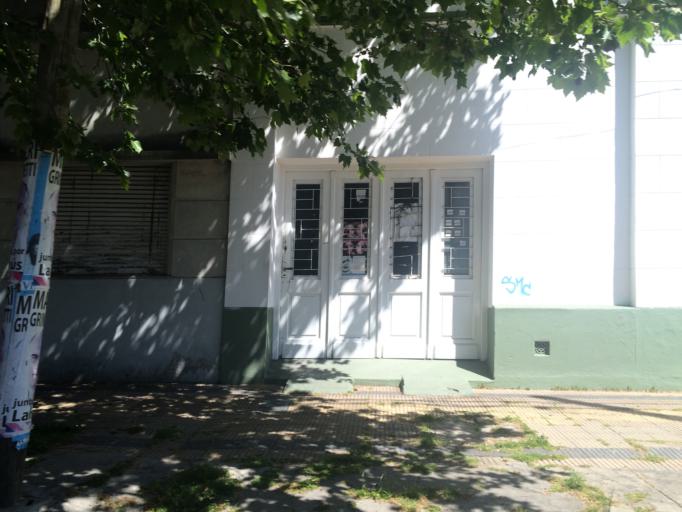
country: AR
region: Buenos Aires
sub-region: Partido de Lanus
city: Lanus
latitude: -34.7167
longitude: -58.3981
